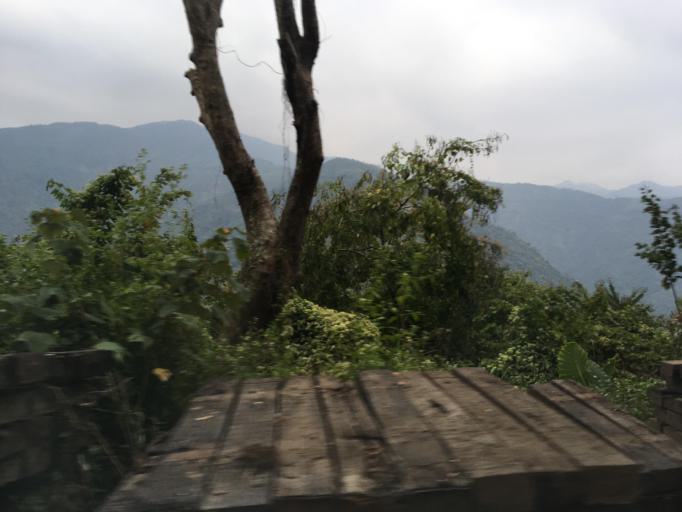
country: TW
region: Taiwan
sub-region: Chiayi
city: Jiayi Shi
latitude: 23.5351
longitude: 120.6085
